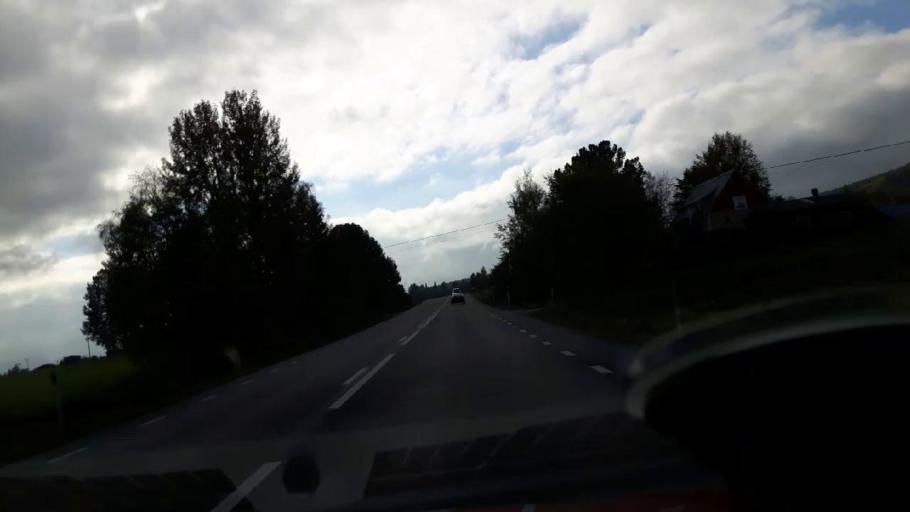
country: SE
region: Gaevleborg
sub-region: Bollnas Kommun
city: Arbra
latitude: 61.5067
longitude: 16.3580
